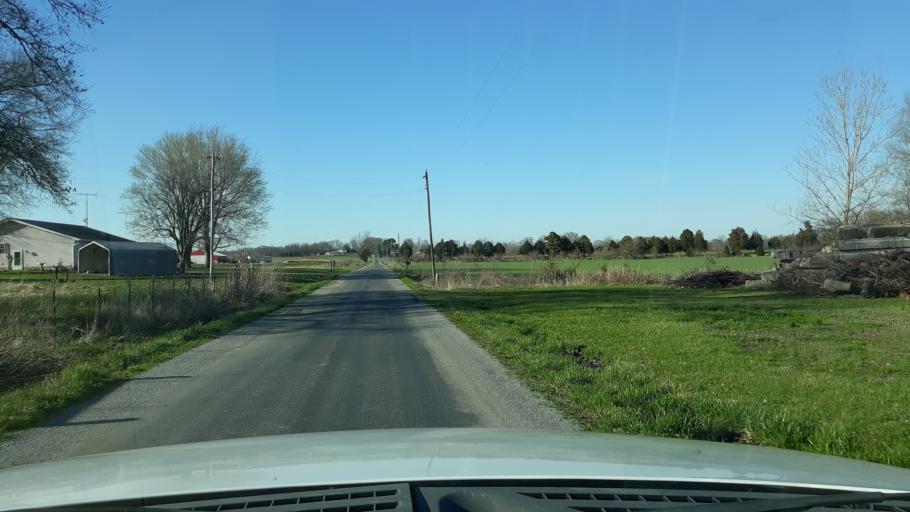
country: US
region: Illinois
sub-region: Saline County
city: Harrisburg
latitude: 37.7971
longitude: -88.6055
